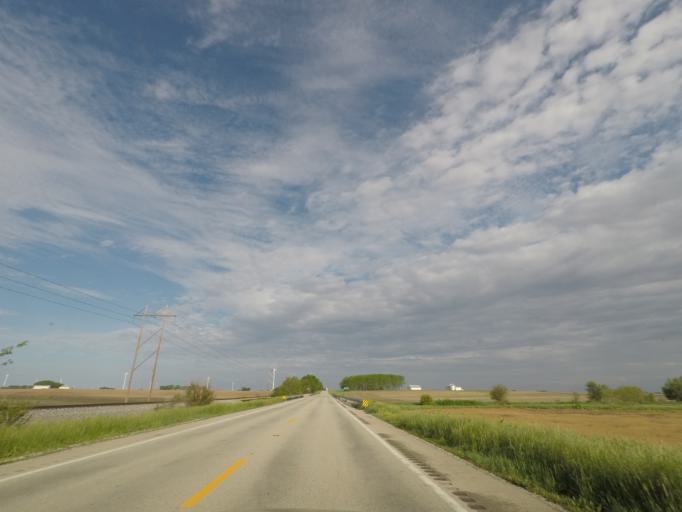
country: US
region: Illinois
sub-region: Logan County
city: Mount Pulaski
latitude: 39.9791
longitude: -89.2037
